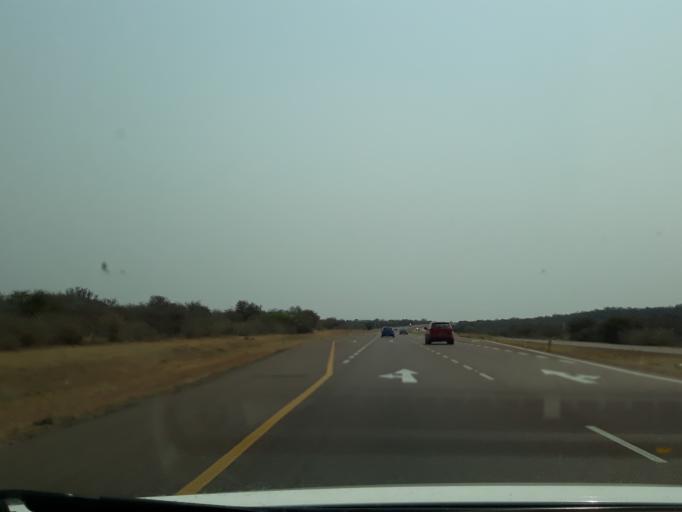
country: BW
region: Kgatleng
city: Bokaa
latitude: -24.4268
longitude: 26.0472
